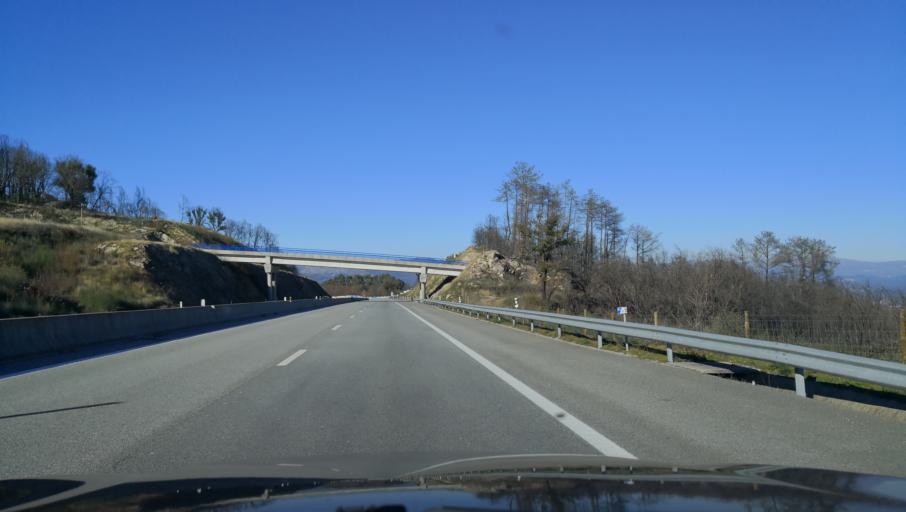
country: PT
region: Viseu
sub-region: Vouzela
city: Vouzela
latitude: 40.6999
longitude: -8.1129
